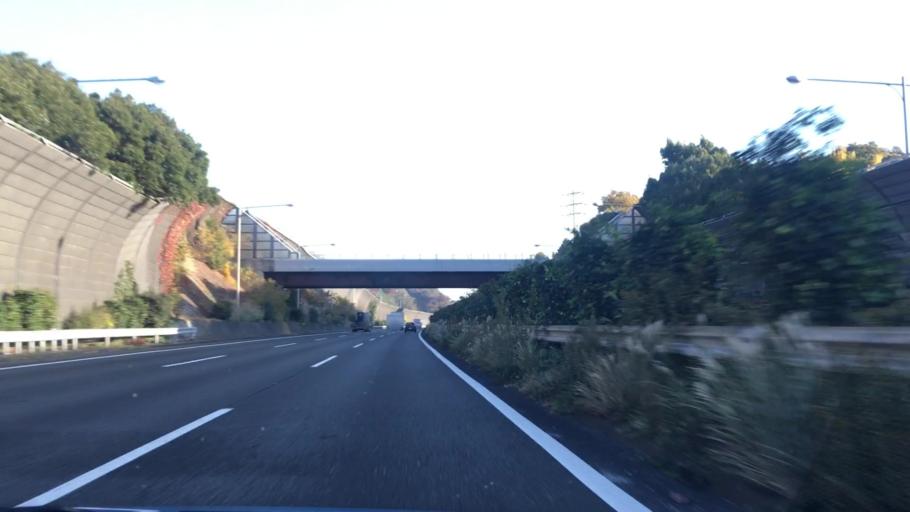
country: JP
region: Kanagawa
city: Isehara
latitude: 35.3790
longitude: 139.2684
